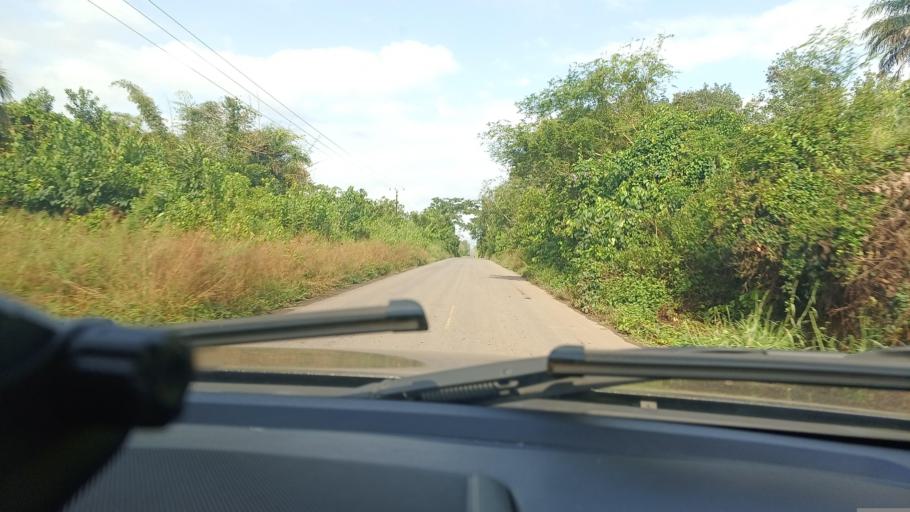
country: LR
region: Bomi
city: Tubmanburg
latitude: 6.6890
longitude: -10.8808
